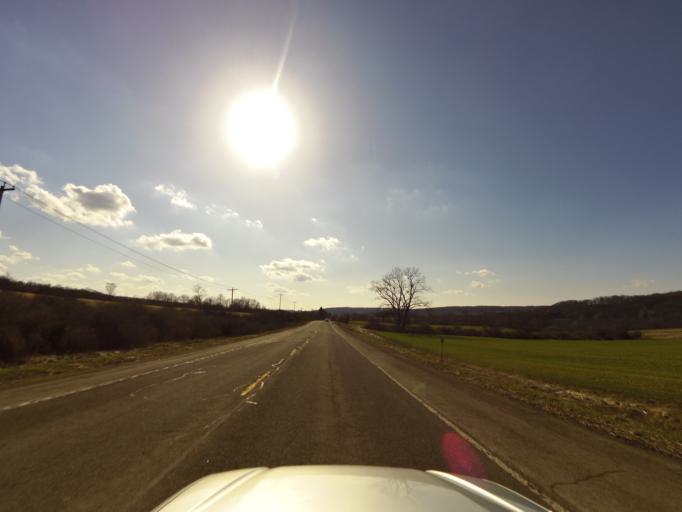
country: US
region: New York
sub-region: Wyoming County
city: Arcade
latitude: 42.4366
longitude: -78.3190
